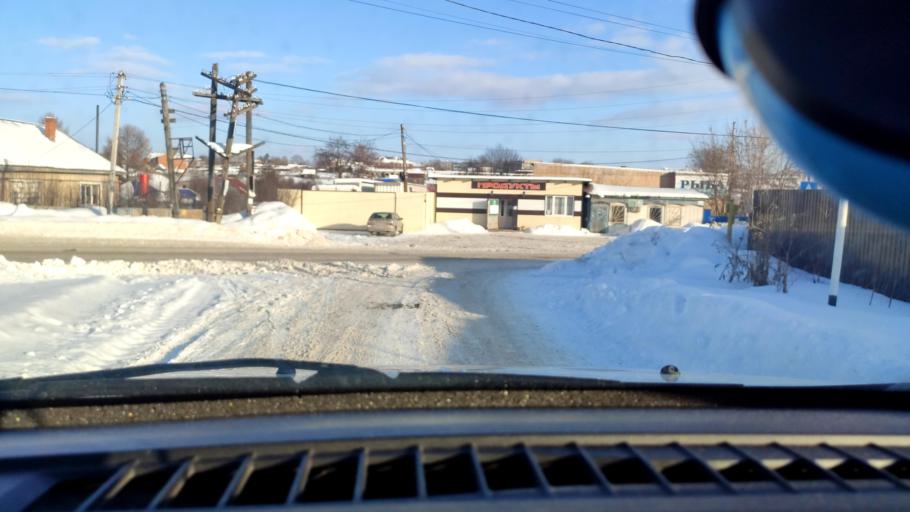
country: RU
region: Perm
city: Kultayevo
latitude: 57.9287
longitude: 55.8766
